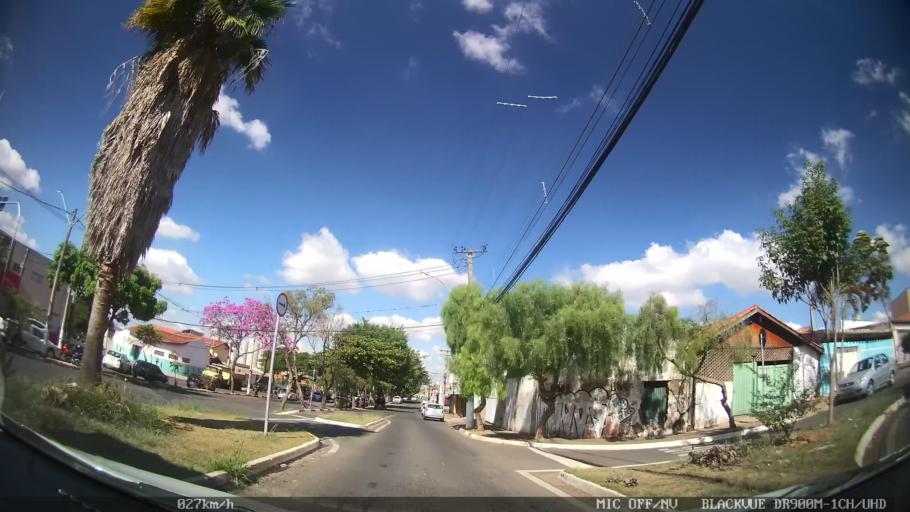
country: BR
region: Sao Paulo
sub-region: Hortolandia
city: Hortolandia
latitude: -22.8915
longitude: -47.2216
